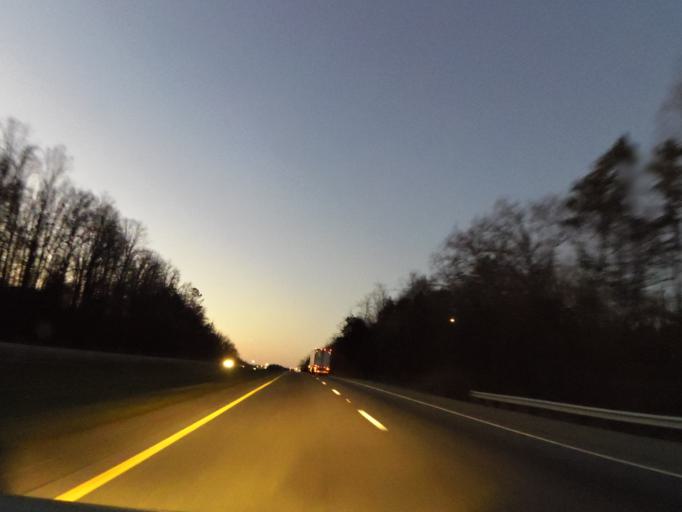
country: US
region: Tennessee
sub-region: Cocke County
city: Newport
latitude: 35.9333
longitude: -83.1941
